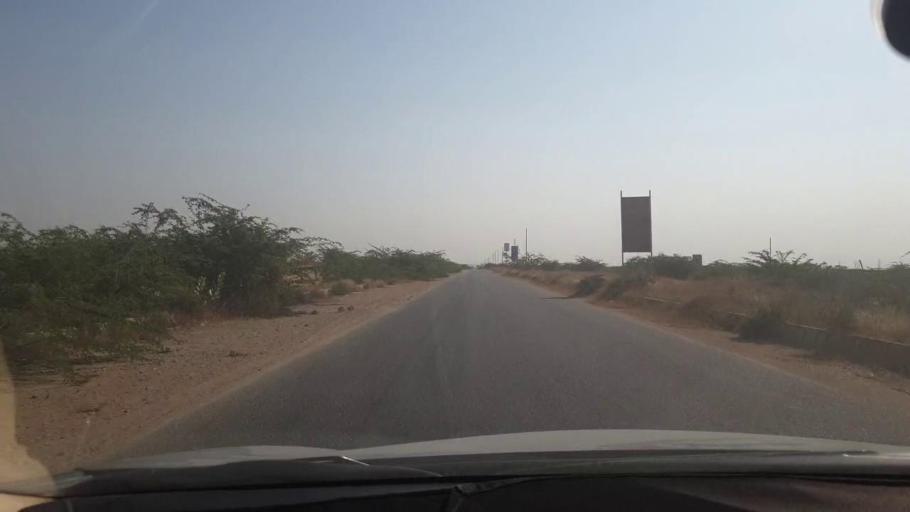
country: PK
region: Sindh
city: Malir Cantonment
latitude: 25.0695
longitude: 67.1387
